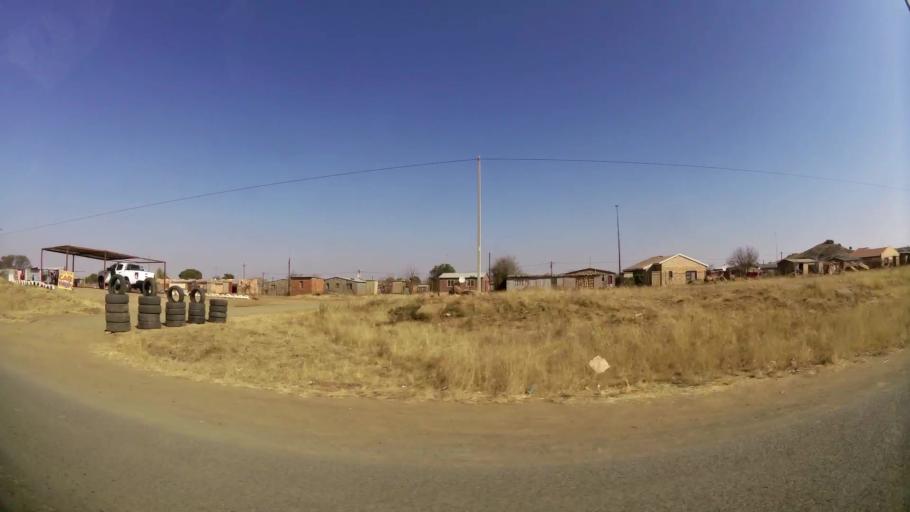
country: ZA
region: Orange Free State
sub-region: Mangaung Metropolitan Municipality
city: Bloemfontein
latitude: -29.1889
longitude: 26.2710
